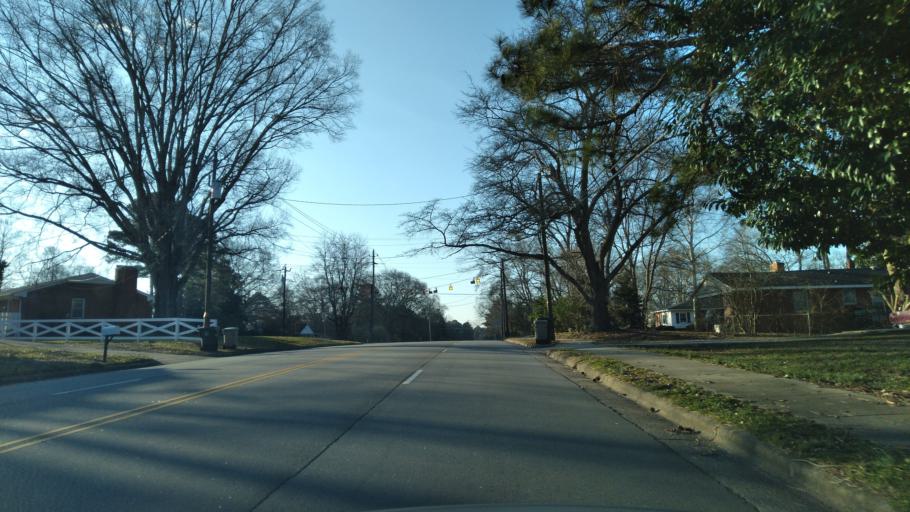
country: US
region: North Carolina
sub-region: Wake County
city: Garner
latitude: 35.7024
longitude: -78.6184
